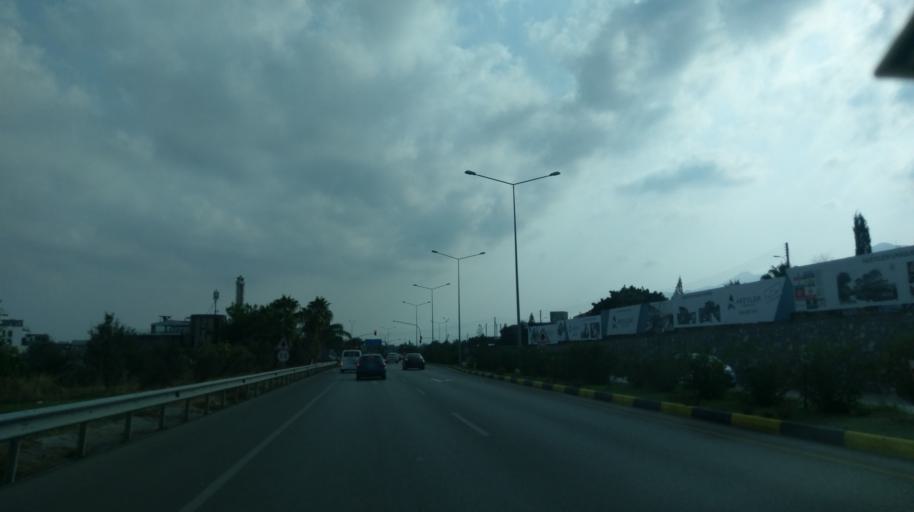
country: CY
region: Keryneia
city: Kyrenia
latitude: 35.3277
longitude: 33.3073
